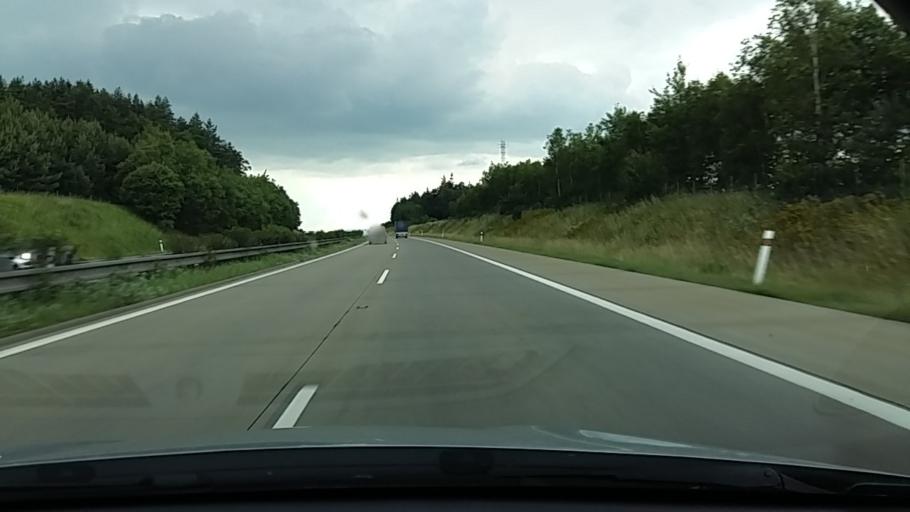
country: CZ
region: Plzensky
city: Bor
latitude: 49.7519
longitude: 12.8073
